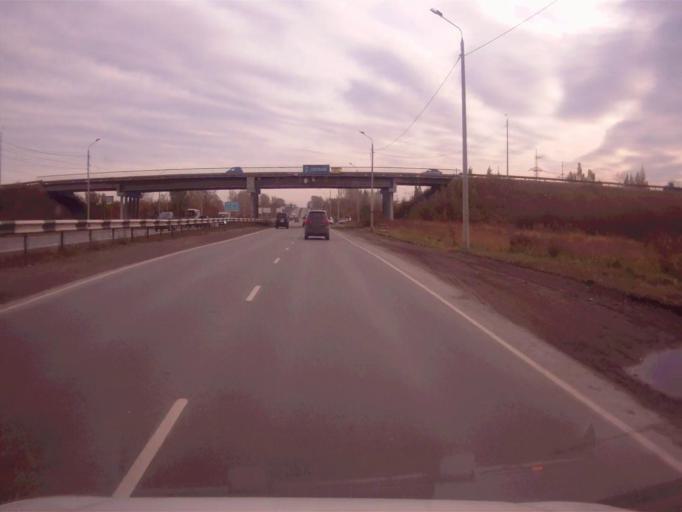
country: RU
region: Chelyabinsk
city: Novosineglazovskiy
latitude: 55.0627
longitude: 61.3993
